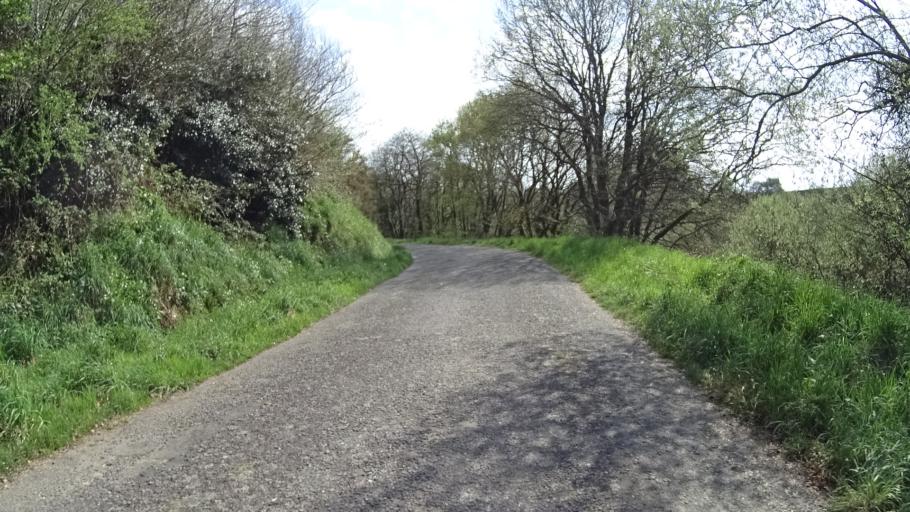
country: FR
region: Brittany
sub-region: Departement du Finistere
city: Sizun
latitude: 48.4190
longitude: -4.0982
